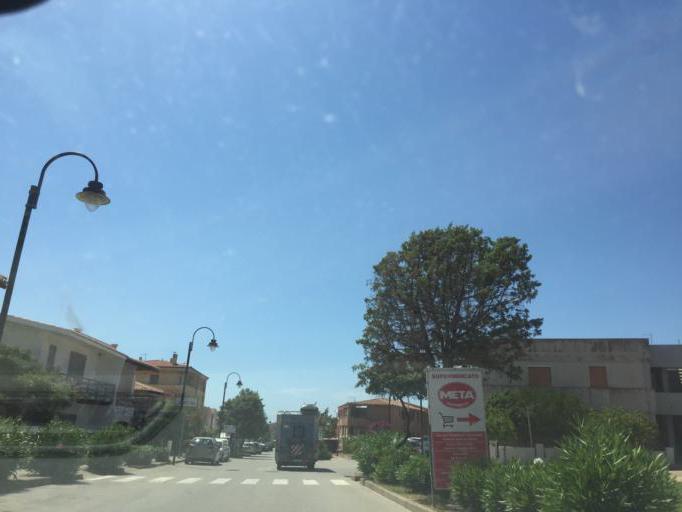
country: IT
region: Sardinia
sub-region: Provincia di Olbia-Tempio
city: Trinita d'Agultu
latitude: 41.0127
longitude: 8.8771
